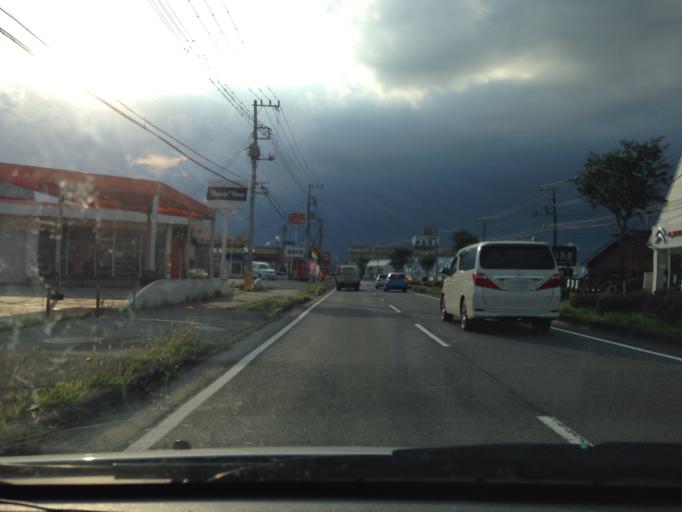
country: JP
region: Ibaraki
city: Naka
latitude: 36.0901
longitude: 140.1460
